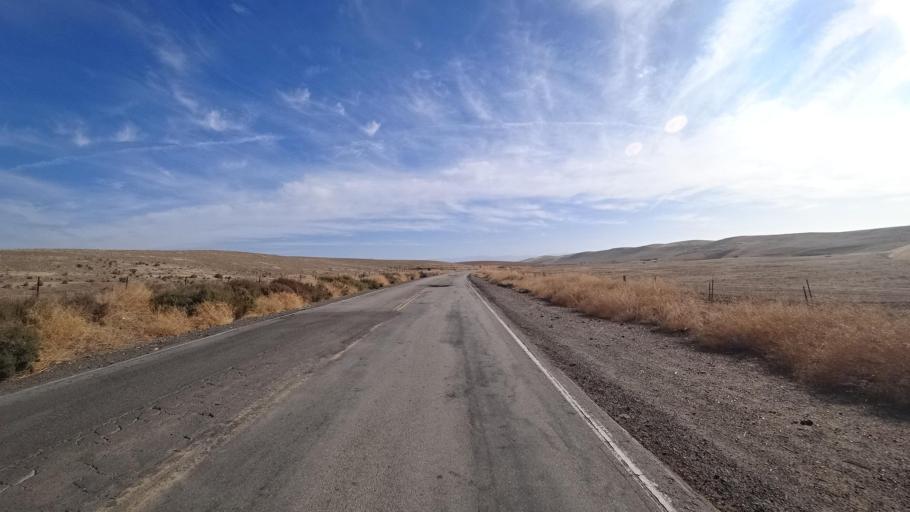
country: US
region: California
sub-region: Tulare County
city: Richgrove
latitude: 35.6196
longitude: -119.0318
